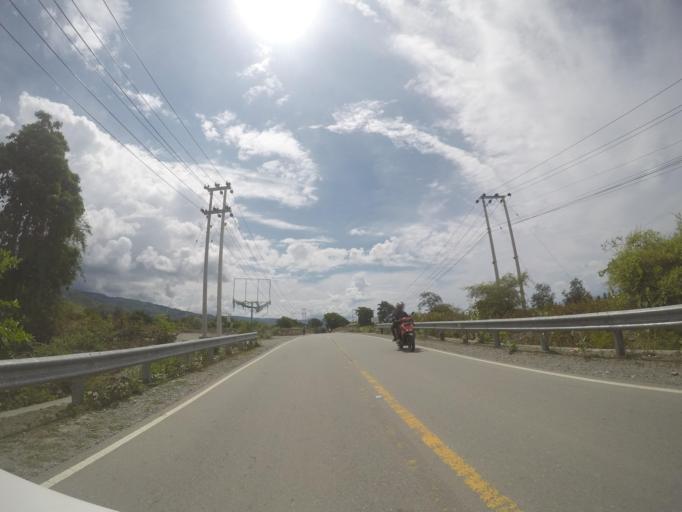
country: TL
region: Liquica
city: Liquica
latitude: -8.5844
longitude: 125.3538
